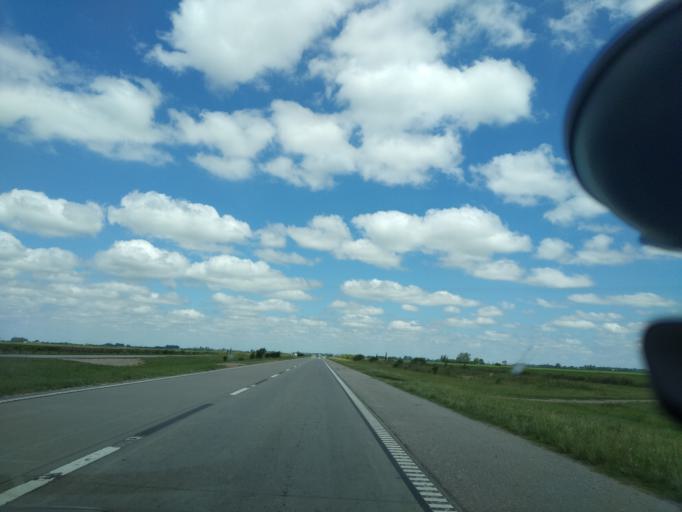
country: AR
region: Cordoba
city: Tio Pujio
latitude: -32.3157
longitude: -63.2768
